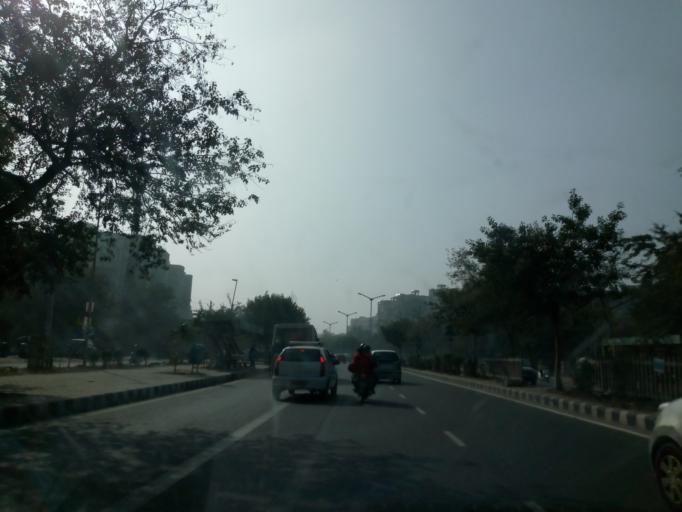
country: IN
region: NCT
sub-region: West Delhi
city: Nangloi Jat
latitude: 28.6046
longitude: 77.0466
